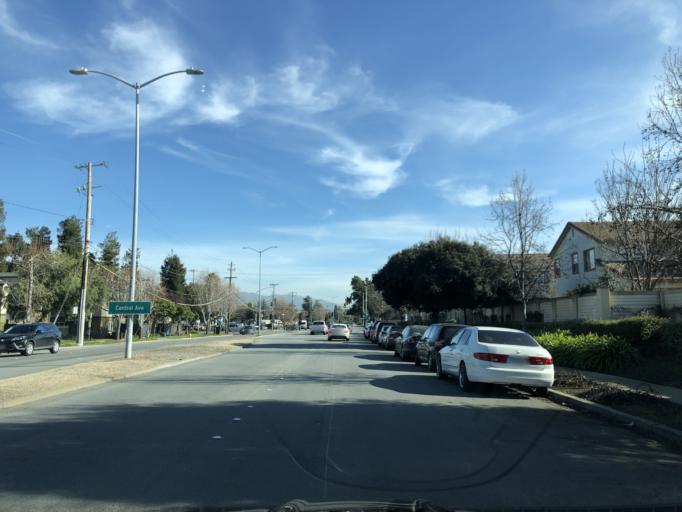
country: US
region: California
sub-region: Alameda County
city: Fremont
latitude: 37.5449
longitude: -122.0152
